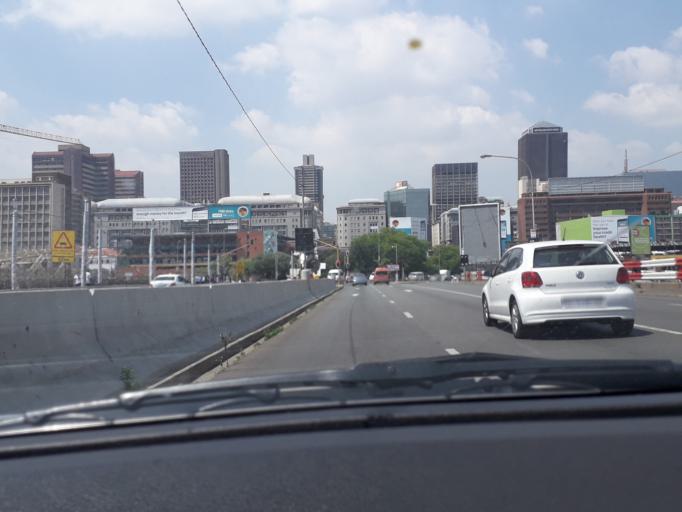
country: ZA
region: Gauteng
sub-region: City of Johannesburg Metropolitan Municipality
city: Johannesburg
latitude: -26.1980
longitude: 28.0376
